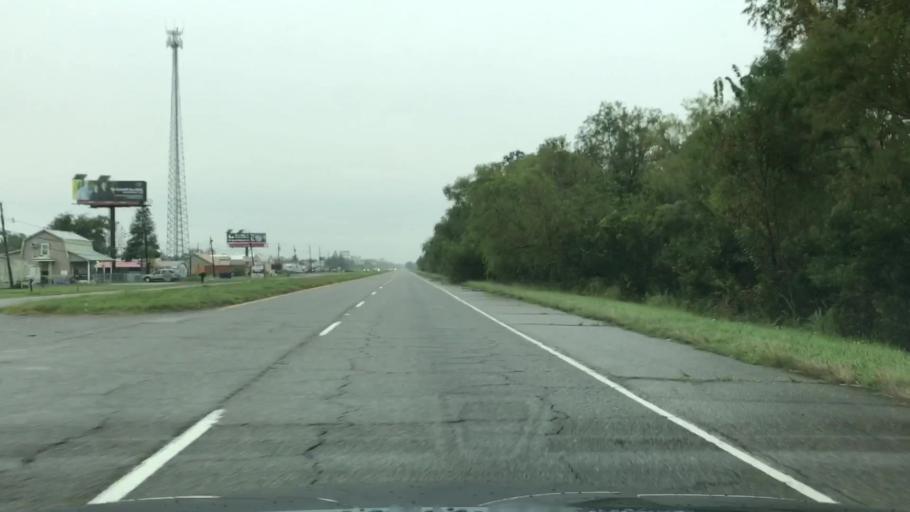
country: US
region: Louisiana
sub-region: Saint Charles Parish
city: Des Allemands
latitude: 29.8099
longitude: -90.4939
